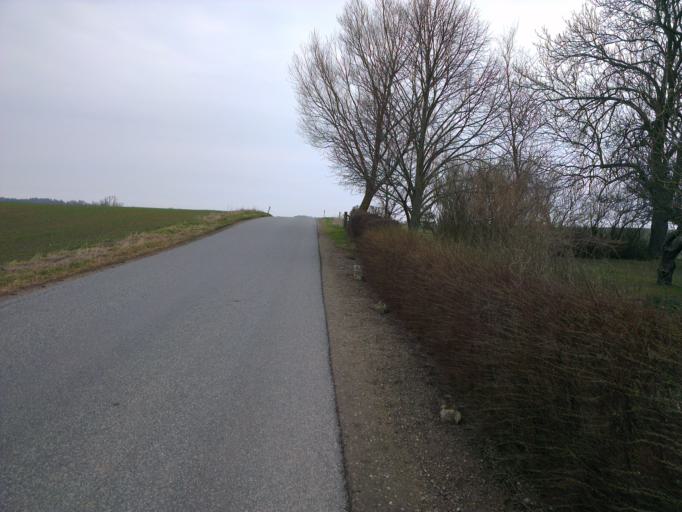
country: DK
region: Capital Region
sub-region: Frederikssund Kommune
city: Skibby
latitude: 55.7467
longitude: 11.9021
